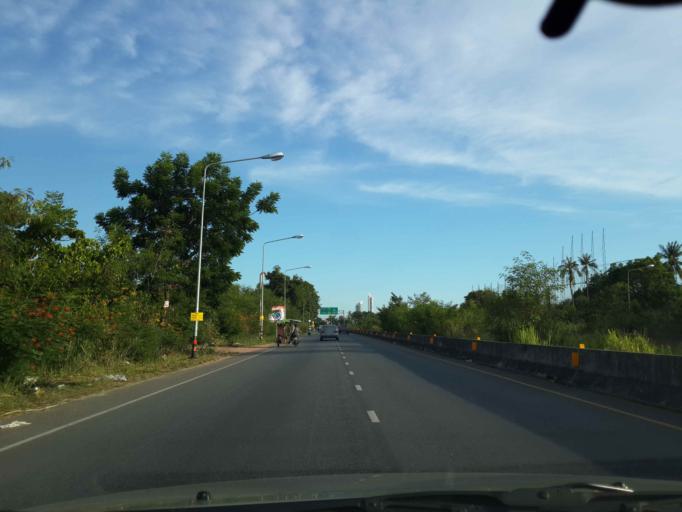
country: TH
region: Chon Buri
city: Phatthaya
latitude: 12.8975
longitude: 100.9003
